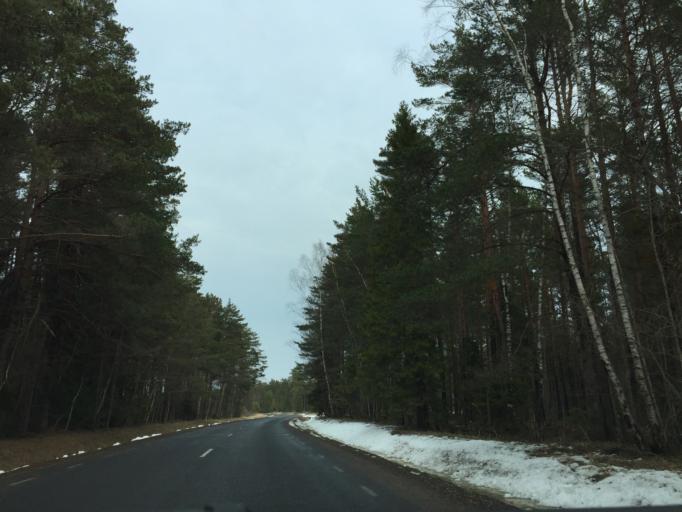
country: EE
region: Saare
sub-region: Kuressaare linn
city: Kuressaare
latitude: 58.5847
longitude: 22.5641
